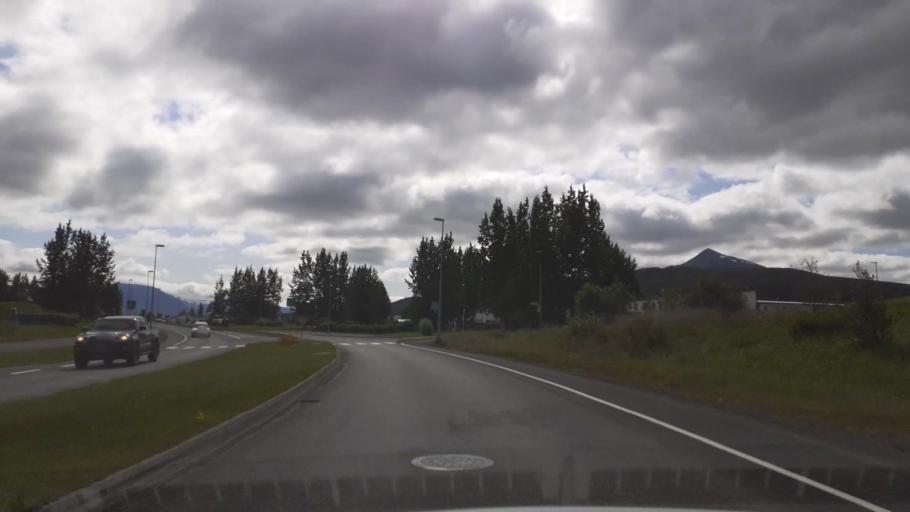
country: IS
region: Northeast
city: Akureyri
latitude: 65.6805
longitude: -18.1164
